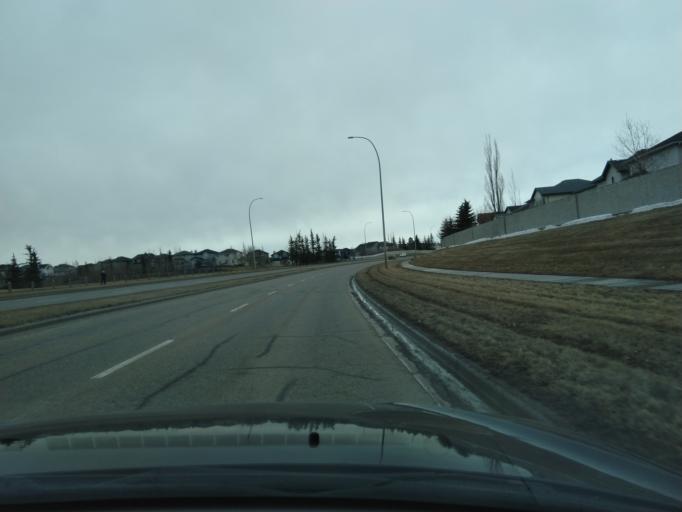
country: CA
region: Alberta
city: Calgary
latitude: 51.1433
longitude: -114.1895
